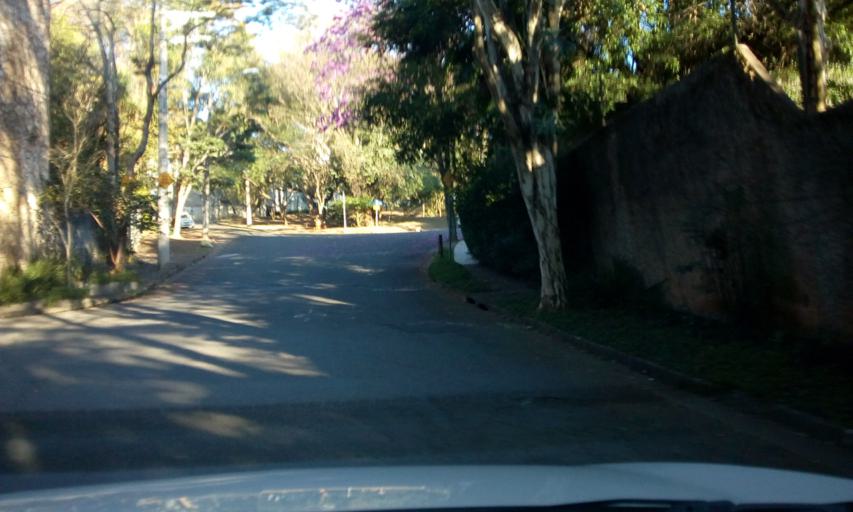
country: BR
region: Sao Paulo
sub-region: Sao Paulo
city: Sao Paulo
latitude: -23.5967
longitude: -46.7027
